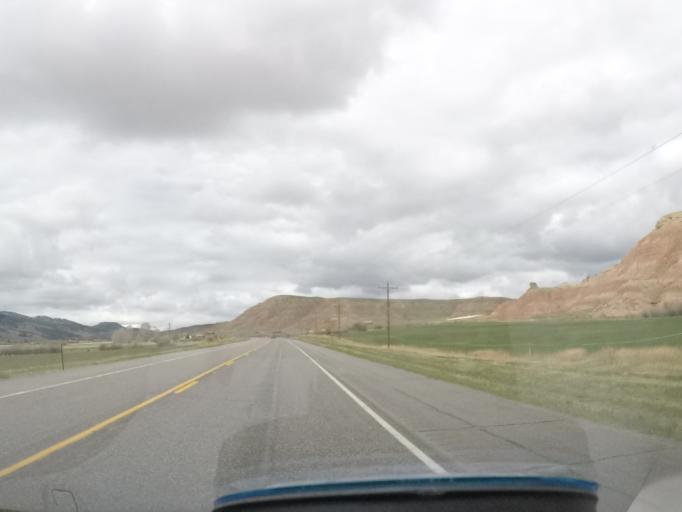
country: US
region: Wyoming
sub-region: Sublette County
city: Pinedale
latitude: 43.5637
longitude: -109.7013
